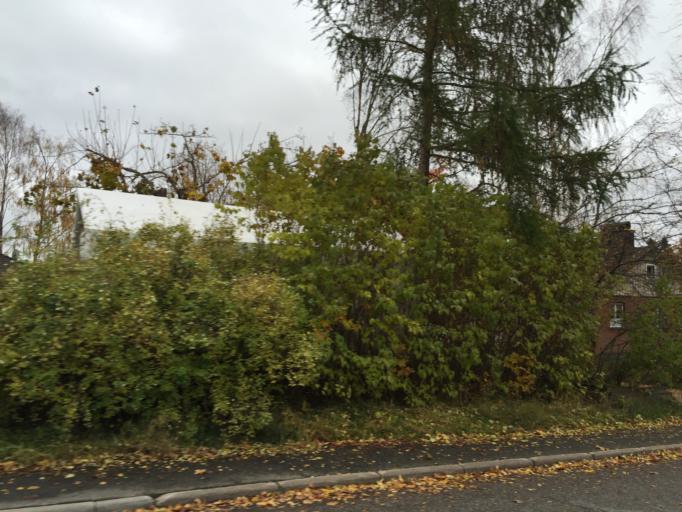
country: SE
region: Stockholm
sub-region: Salems Kommun
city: Ronninge
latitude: 59.2001
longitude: 17.7316
